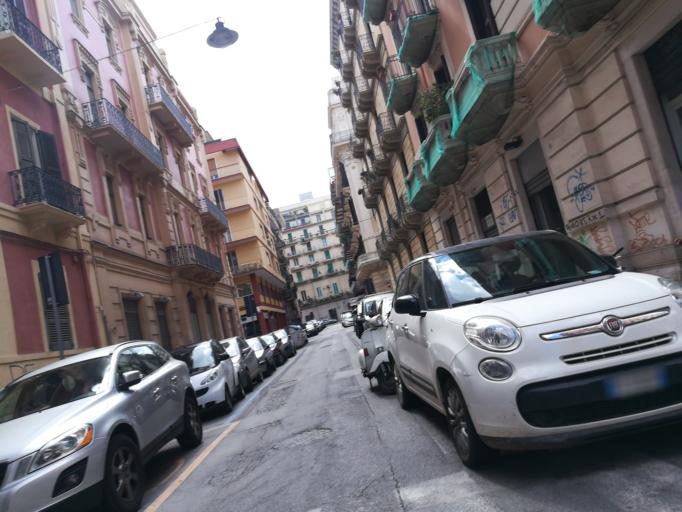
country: IT
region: Apulia
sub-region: Provincia di Bari
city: Bari
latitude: 41.1228
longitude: 16.8745
